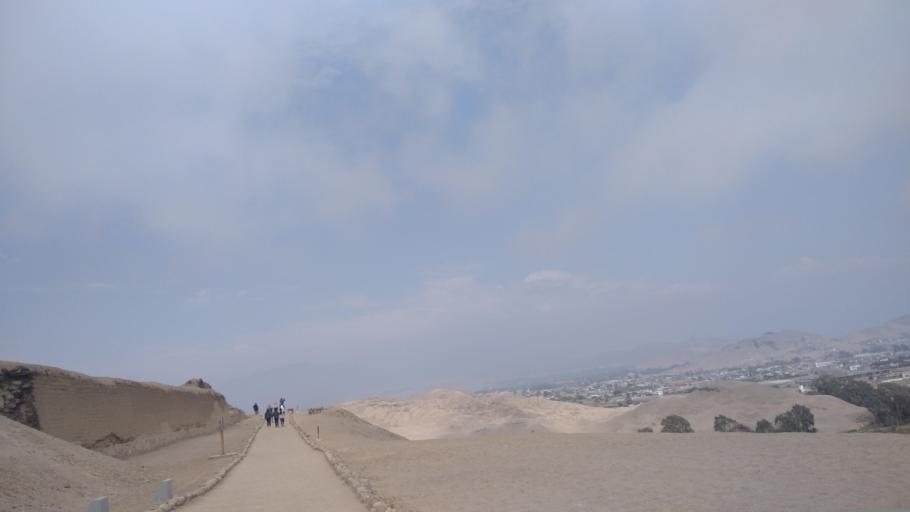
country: PE
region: Lima
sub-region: Lima
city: Punta Hermosa
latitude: -12.2643
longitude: -76.9018
